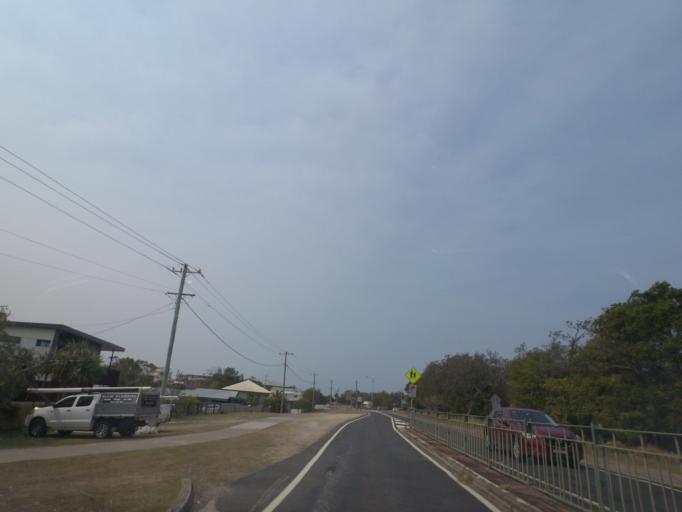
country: AU
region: New South Wales
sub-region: Tweed
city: Casuarina
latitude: -28.3377
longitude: 153.5735
